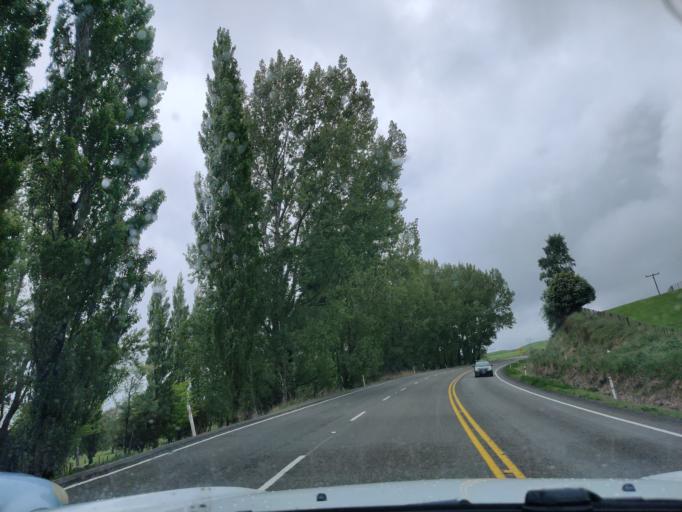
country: NZ
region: Manawatu-Wanganui
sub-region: Ruapehu District
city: Waiouru
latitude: -39.5361
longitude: 175.6800
